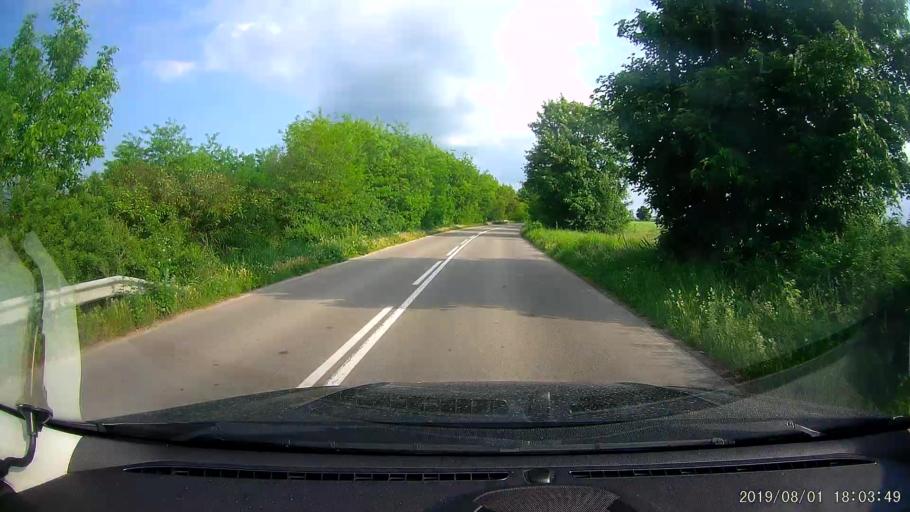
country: BG
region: Silistra
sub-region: Obshtina Alfatar
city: Alfatar
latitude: 43.9187
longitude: 27.2903
